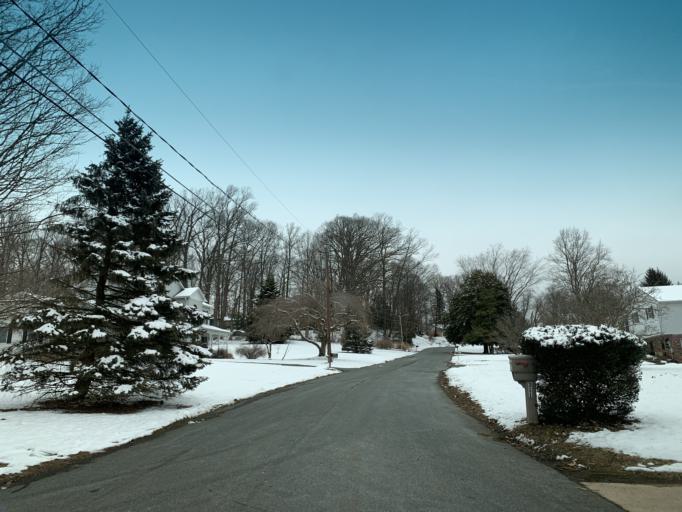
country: US
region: Maryland
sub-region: Harford County
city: Aberdeen
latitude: 39.5588
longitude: -76.1696
